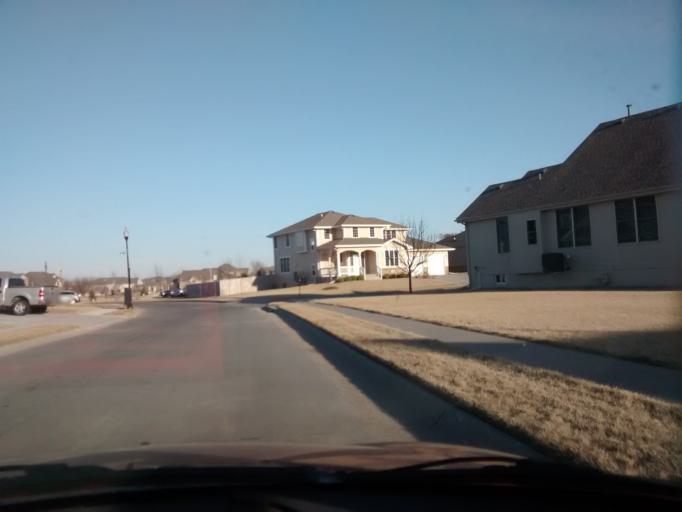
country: US
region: Nebraska
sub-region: Sarpy County
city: Papillion
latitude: 41.1450
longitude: -95.9811
